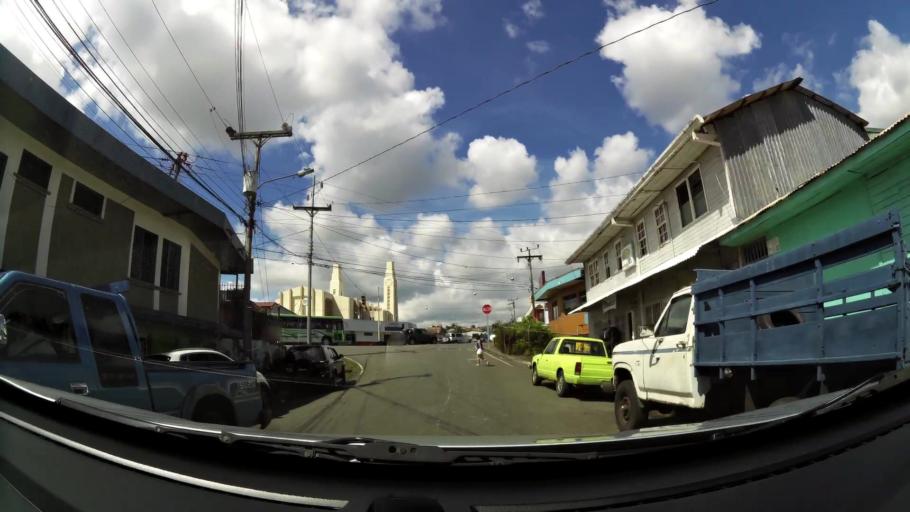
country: CR
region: San Jose
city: San Isidro
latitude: 9.3736
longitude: -83.7011
